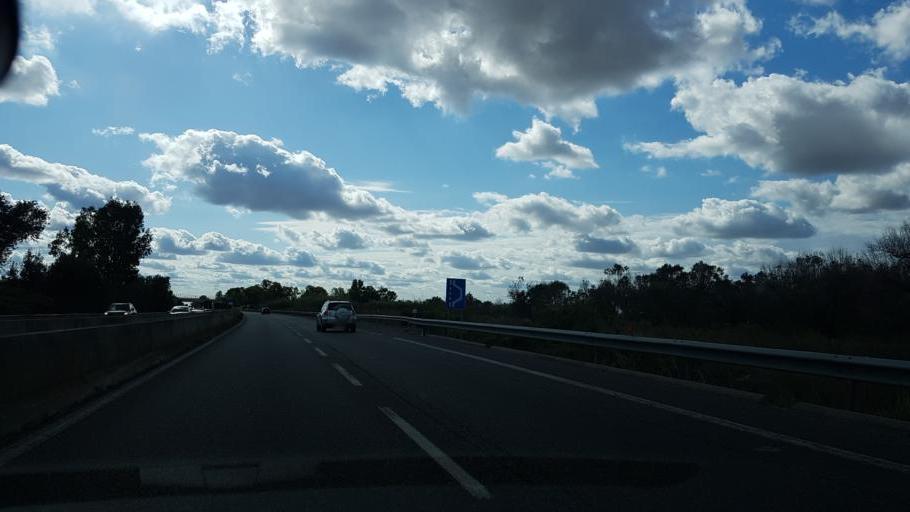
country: IT
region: Apulia
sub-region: Provincia di Brindisi
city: San Pietro Vernotico
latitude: 40.5254
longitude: 18.0136
